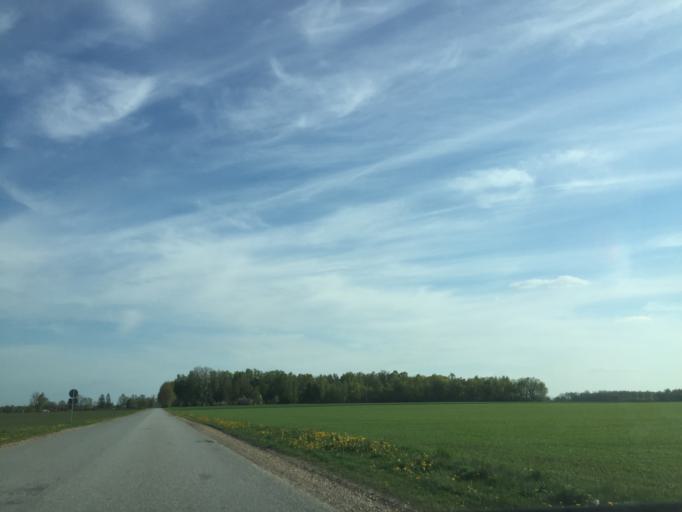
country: LV
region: Bauskas Rajons
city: Bauska
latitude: 56.3501
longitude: 24.2331
